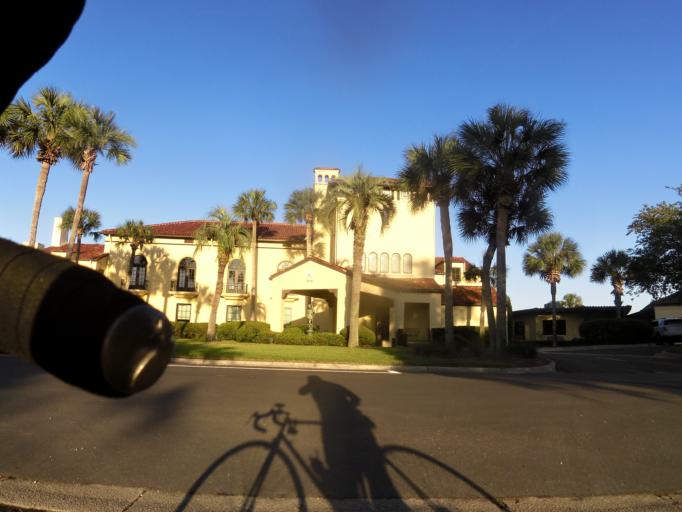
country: US
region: Florida
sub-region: Duval County
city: Jacksonville
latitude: 30.2526
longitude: -81.6902
